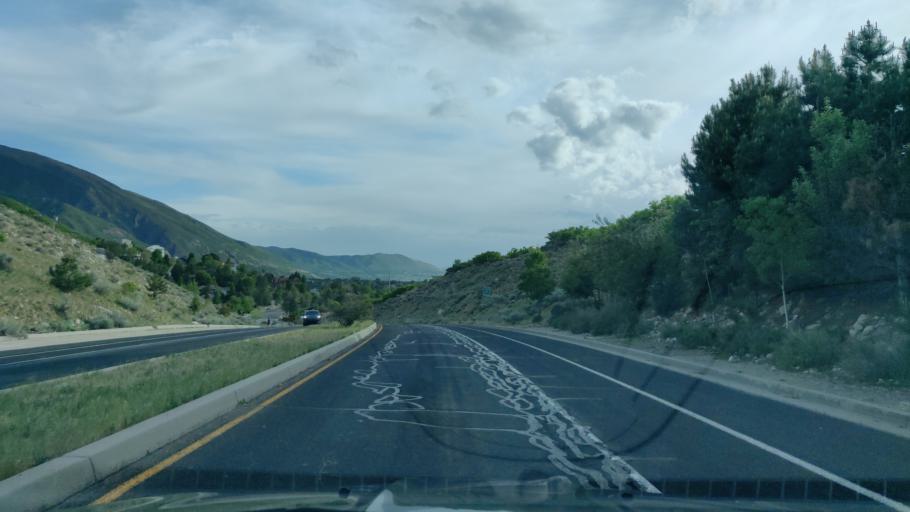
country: US
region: Utah
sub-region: Salt Lake County
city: Granite
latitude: 40.5720
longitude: -111.8001
